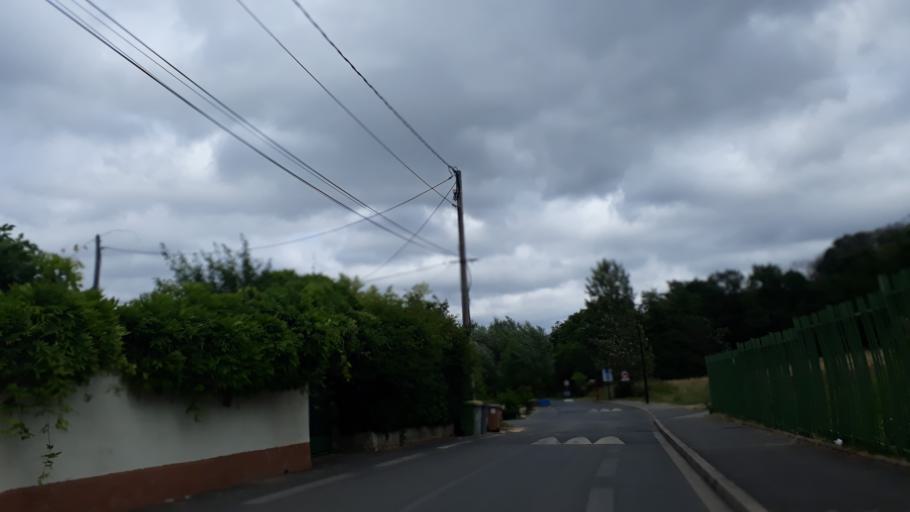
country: FR
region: Ile-de-France
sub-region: Departement de l'Essonne
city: Nozay
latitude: 48.6680
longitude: 2.2564
